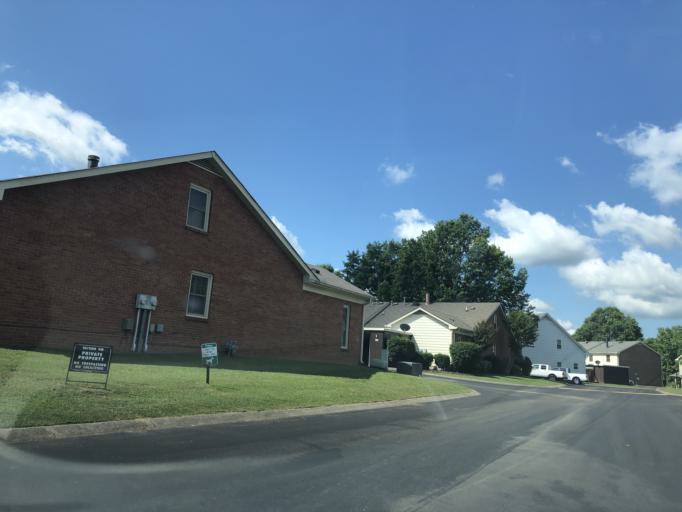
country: US
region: Tennessee
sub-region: Davidson County
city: Belle Meade
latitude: 36.0656
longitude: -86.9437
